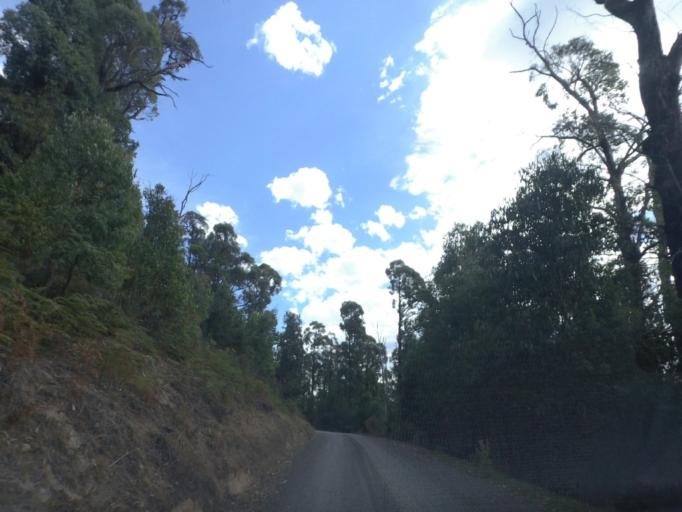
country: AU
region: Victoria
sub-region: Murrindindi
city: Alexandra
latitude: -37.4247
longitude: 145.7602
